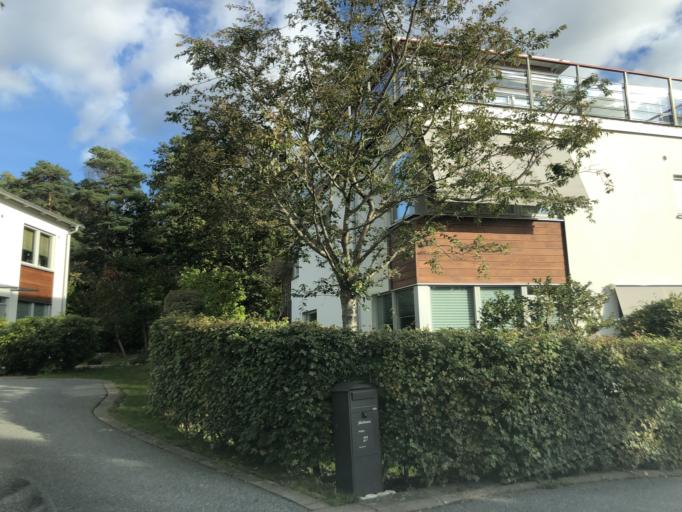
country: SE
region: Vaestra Goetaland
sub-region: Goteborg
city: Billdal
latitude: 57.6271
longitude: 11.9495
